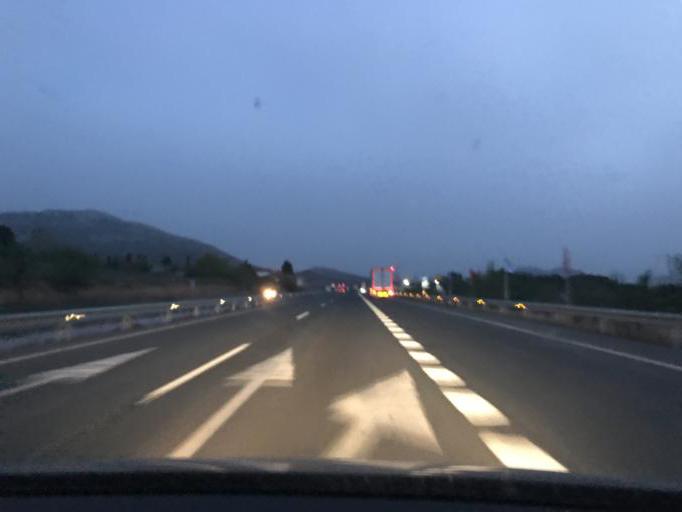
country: ES
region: Andalusia
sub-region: Provincia de Granada
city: Gor
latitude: 37.4174
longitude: -2.9182
